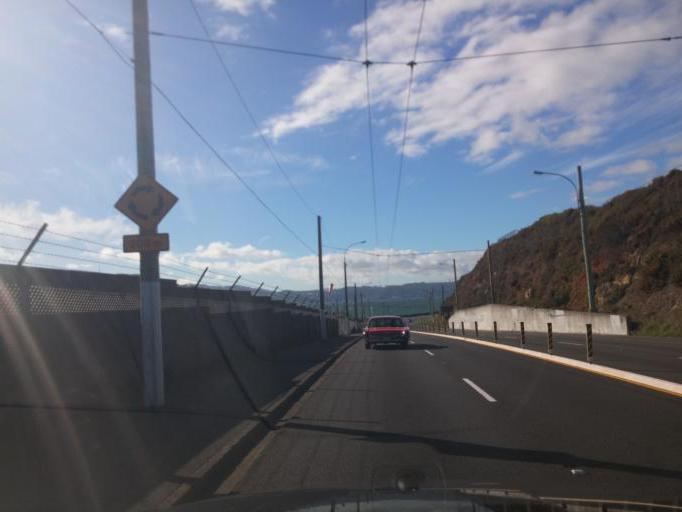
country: NZ
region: Wellington
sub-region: Wellington City
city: Wellington
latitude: -41.3189
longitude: 174.8093
